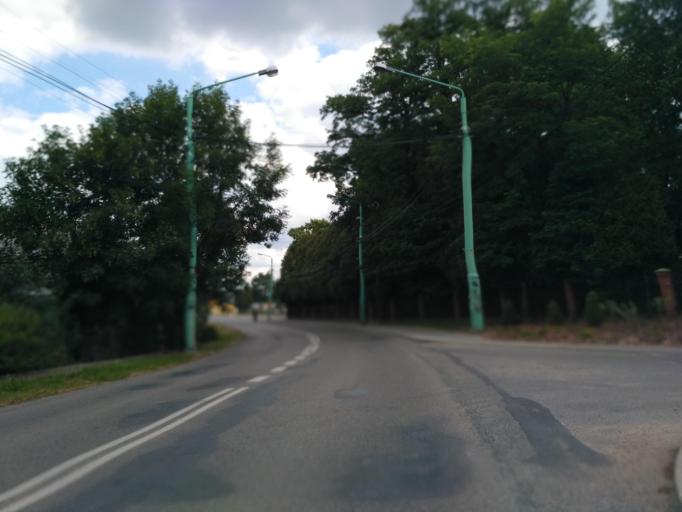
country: PL
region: Subcarpathian Voivodeship
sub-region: Powiat debicki
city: Zyrakow
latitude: 50.0621
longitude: 21.3583
